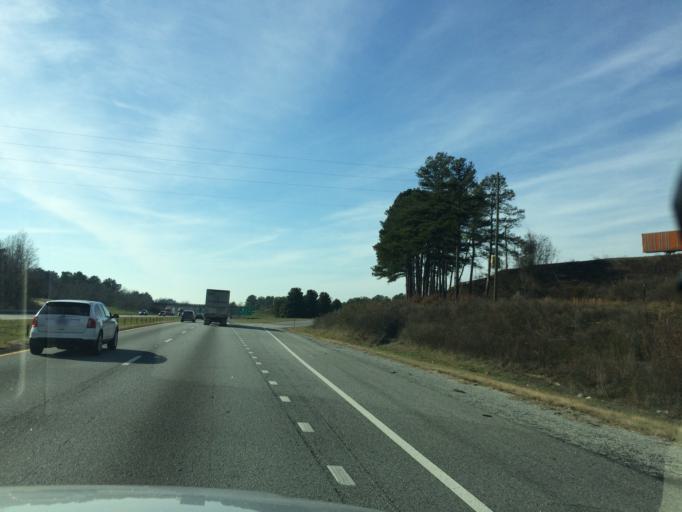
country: US
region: Georgia
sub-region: Hart County
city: Reed Creek
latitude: 34.5011
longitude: -82.9903
